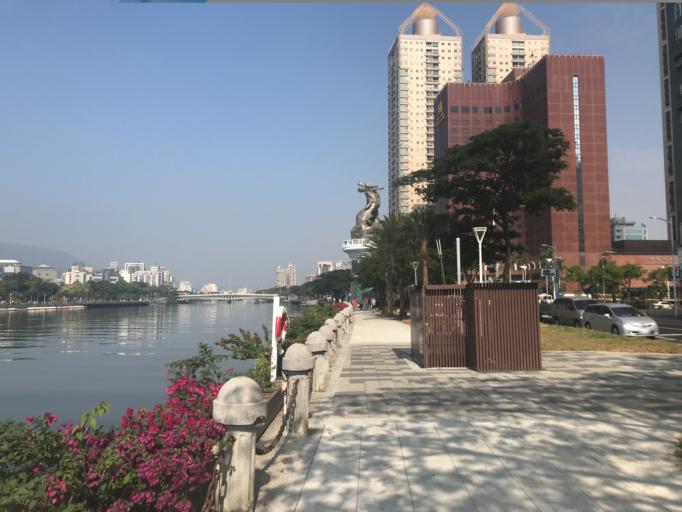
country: TW
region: Kaohsiung
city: Kaohsiung
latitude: 22.6225
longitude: 120.2906
